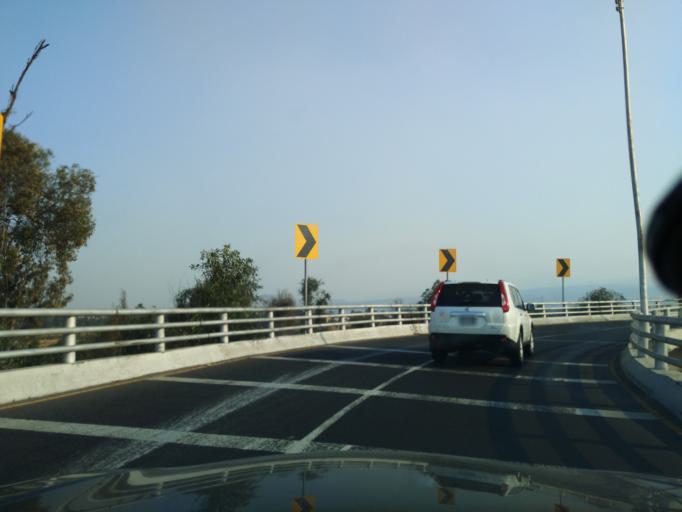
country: MX
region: Mexico City
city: Xochimilco
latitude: 19.2896
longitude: -99.1133
